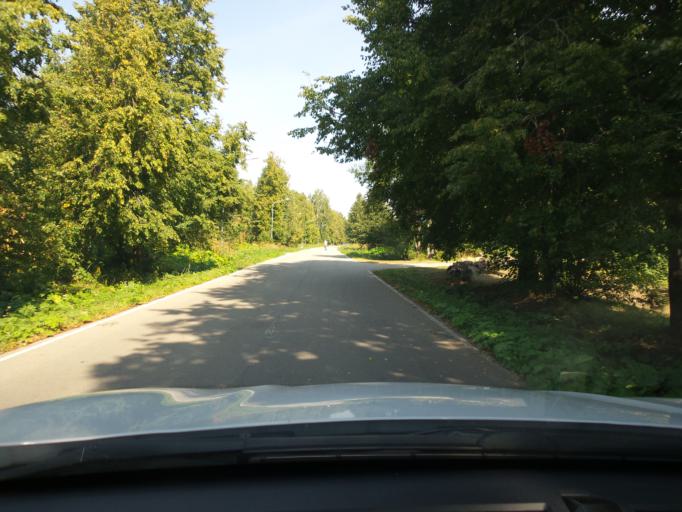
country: LV
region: Tukuma Rajons
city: Tukums
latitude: 56.9303
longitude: 23.2163
